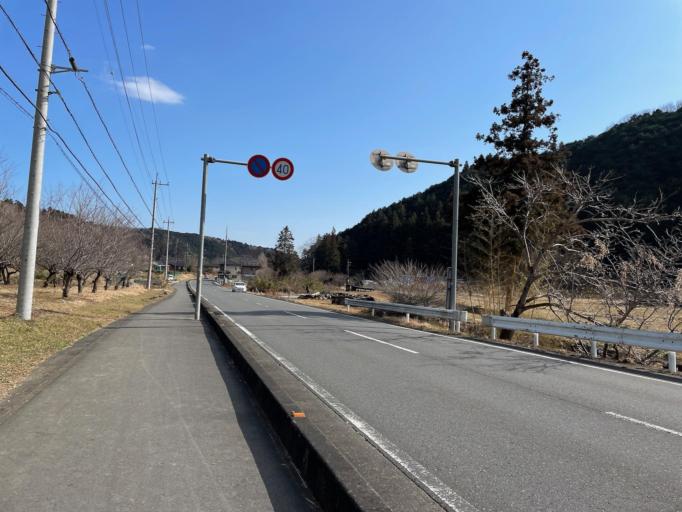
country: JP
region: Saitama
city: Hanno
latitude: 35.8434
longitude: 139.2707
